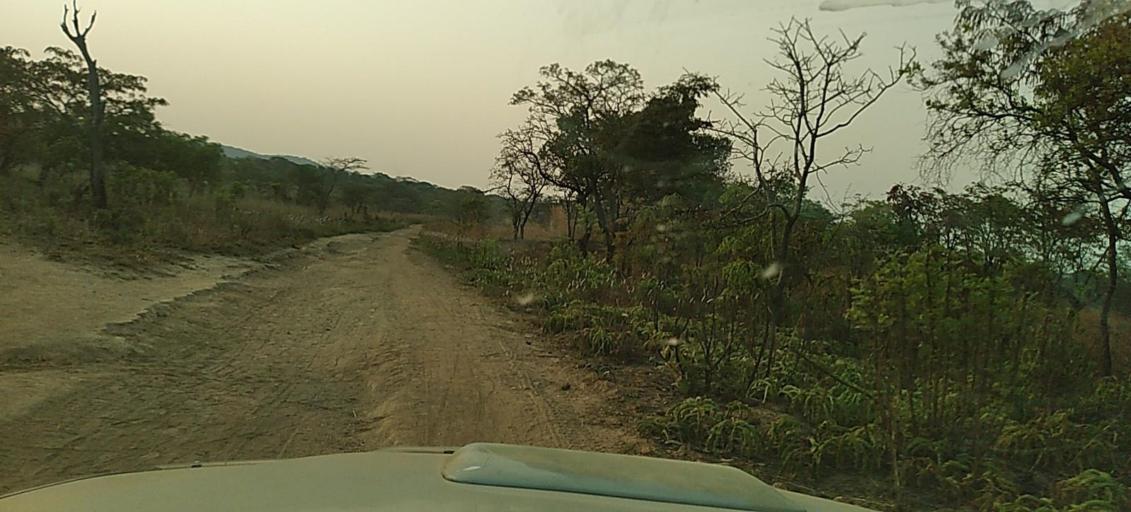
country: ZM
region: North-Western
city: Kasempa
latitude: -13.0714
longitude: 26.3830
